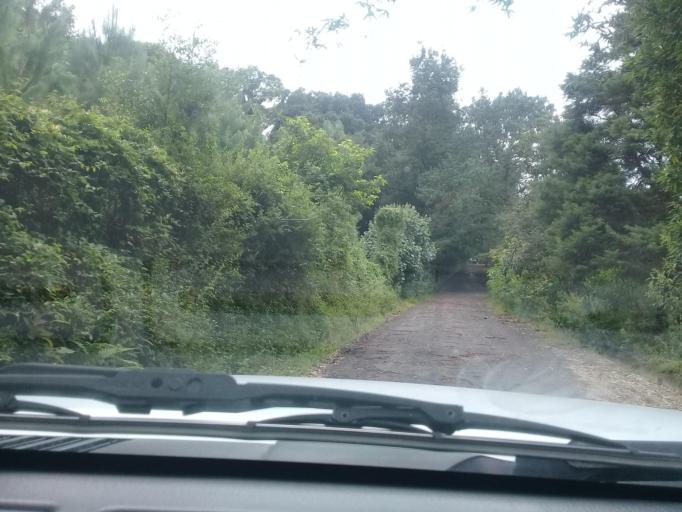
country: MX
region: Veracruz
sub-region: Rafael Lucio
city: Piletas
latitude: 19.5866
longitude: -96.9677
